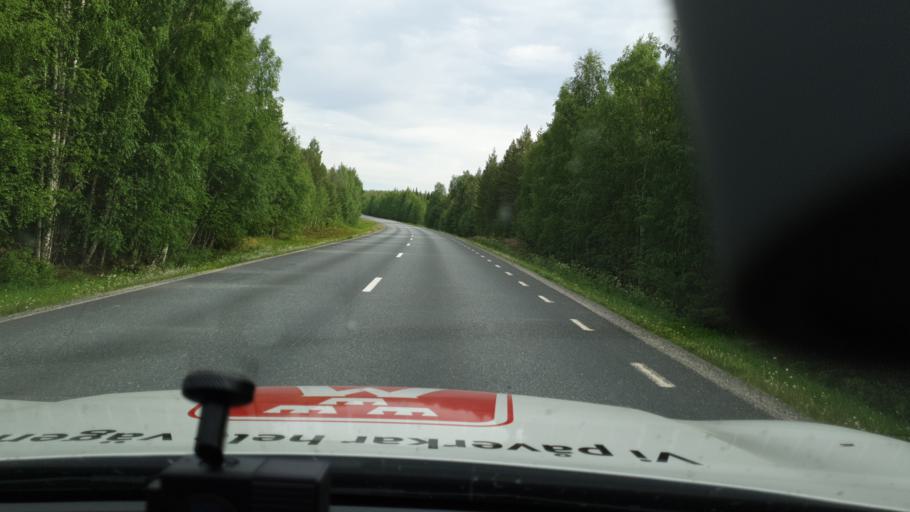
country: SE
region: Vaesterbotten
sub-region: Lycksele Kommun
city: Lycksele
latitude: 64.7788
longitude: 18.7342
